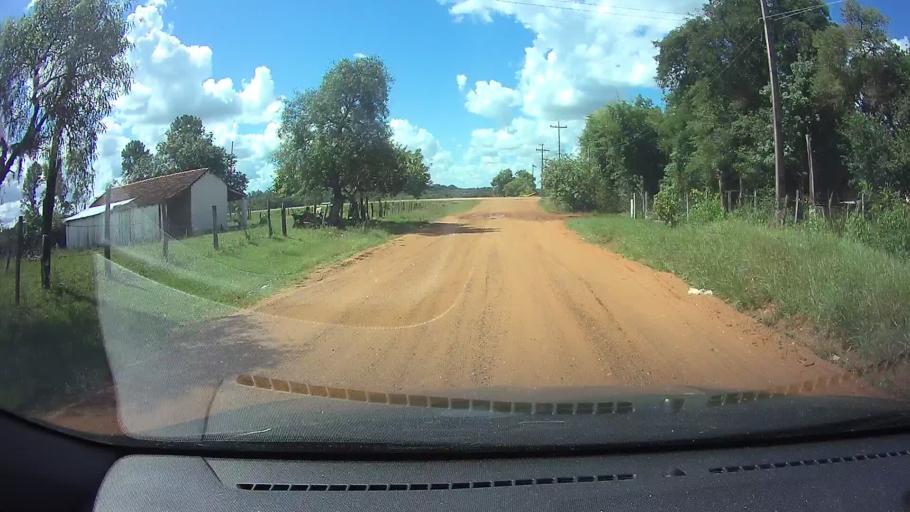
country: PY
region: Paraguari
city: La Colmena
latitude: -25.8990
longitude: -56.7926
